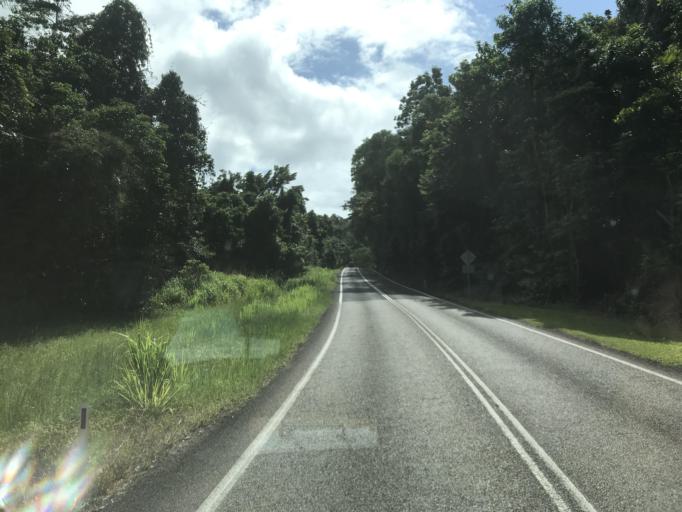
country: AU
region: Queensland
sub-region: Cassowary Coast
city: Innisfail
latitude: -17.8676
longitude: 146.0686
